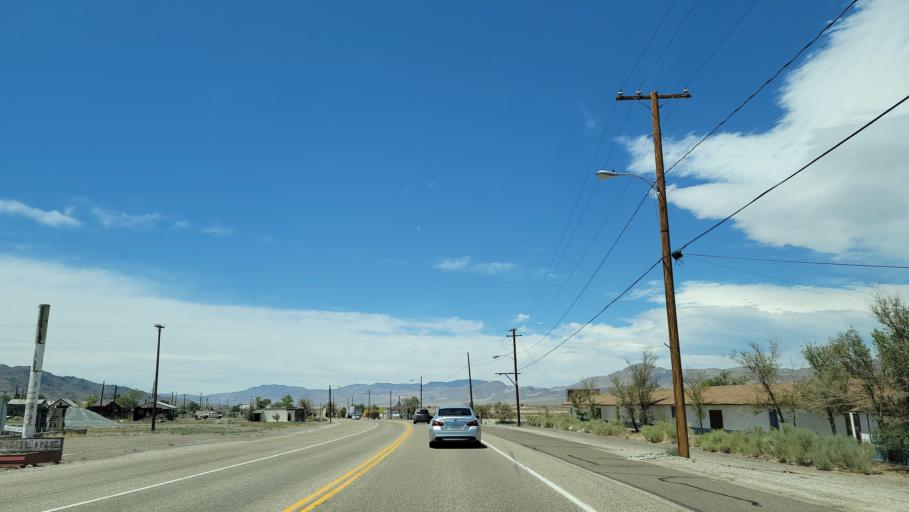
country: US
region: Nevada
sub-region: Mineral County
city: Hawthorne
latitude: 38.3875
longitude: -118.1072
